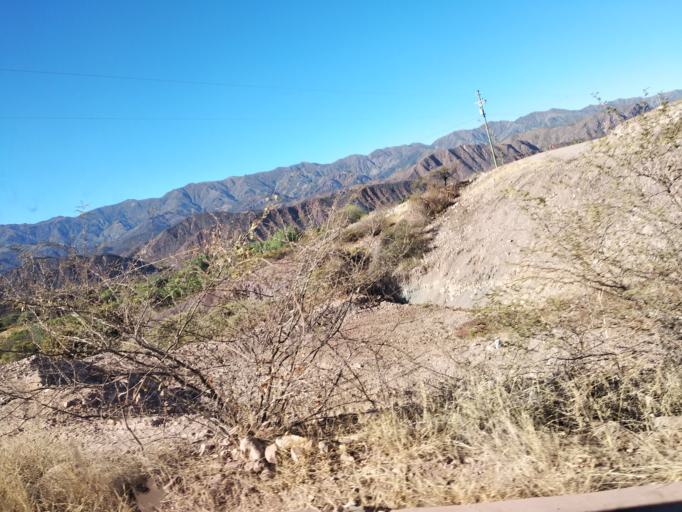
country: BO
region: Cochabamba
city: Mizque
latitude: -18.0780
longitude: -65.7457
